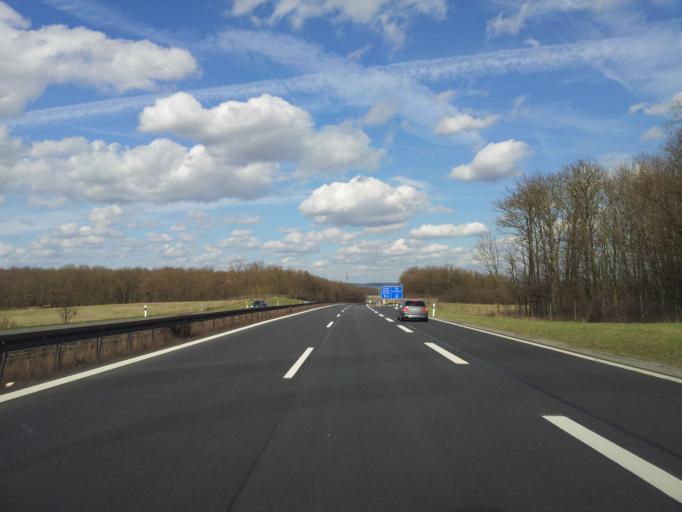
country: DE
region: Bavaria
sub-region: Regierungsbezirk Unterfranken
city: Bergrheinfeld
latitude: 50.0139
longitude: 10.1586
